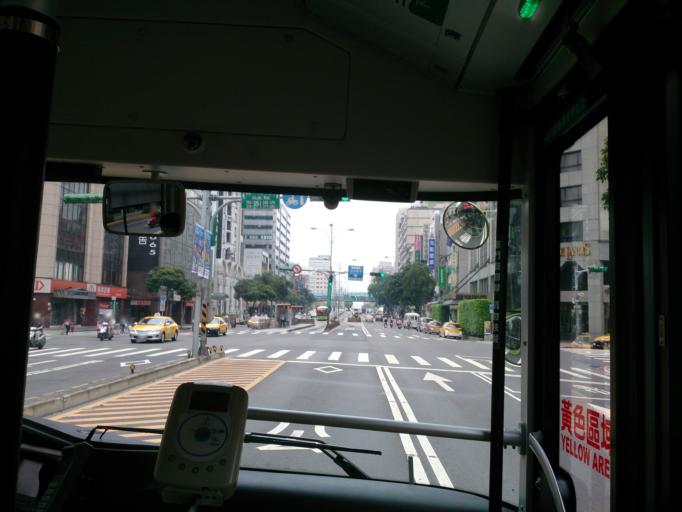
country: TW
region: Taipei
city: Taipei
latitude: 25.0626
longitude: 121.5308
